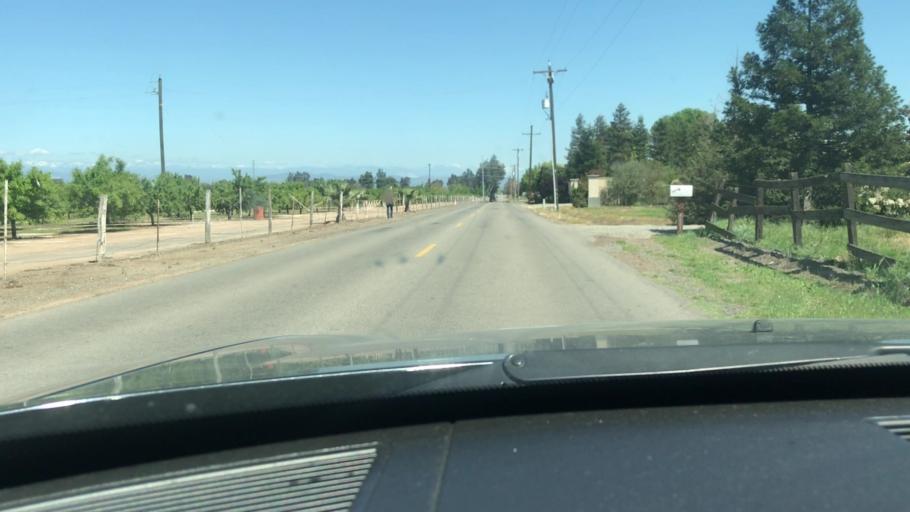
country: US
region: California
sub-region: Fresno County
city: Clovis
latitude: 36.8811
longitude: -119.7004
